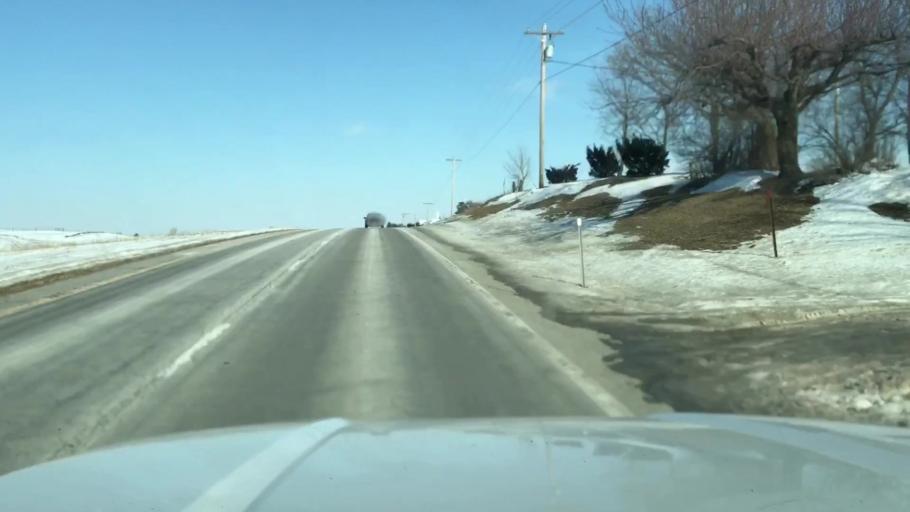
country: US
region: Missouri
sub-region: Andrew County
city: Savannah
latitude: 40.0120
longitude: -94.8795
